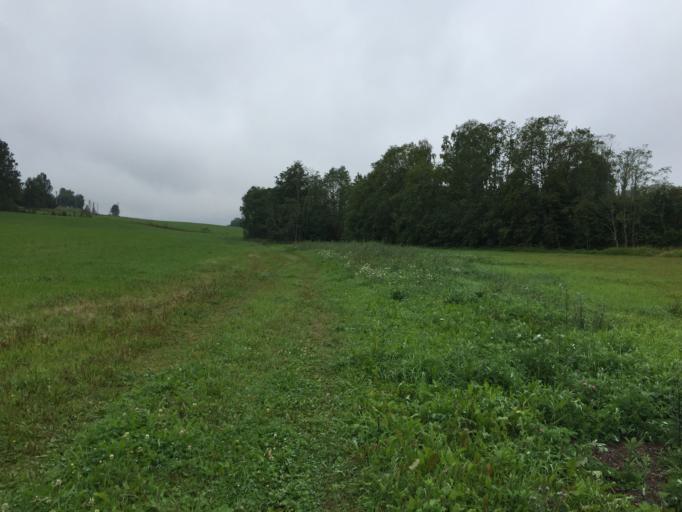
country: NO
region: Akershus
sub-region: Baerum
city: Lysaker
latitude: 59.9841
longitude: 10.6199
